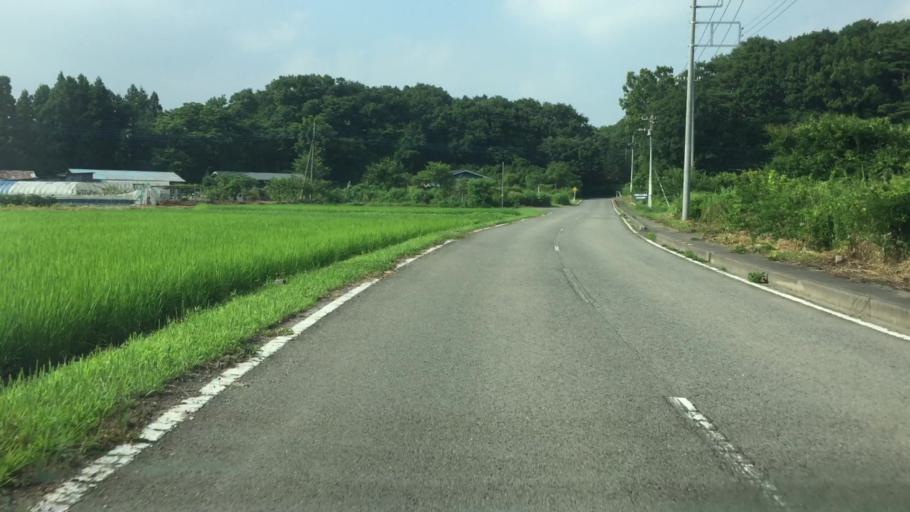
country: JP
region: Tochigi
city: Kuroiso
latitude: 37.0375
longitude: 140.0272
